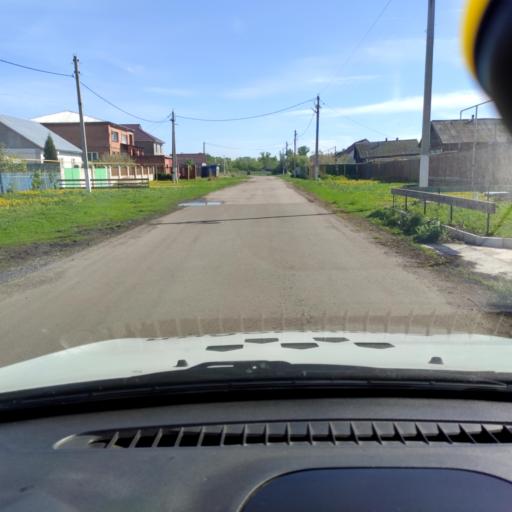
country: RU
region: Samara
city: Tol'yatti
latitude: 53.6672
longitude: 49.4314
